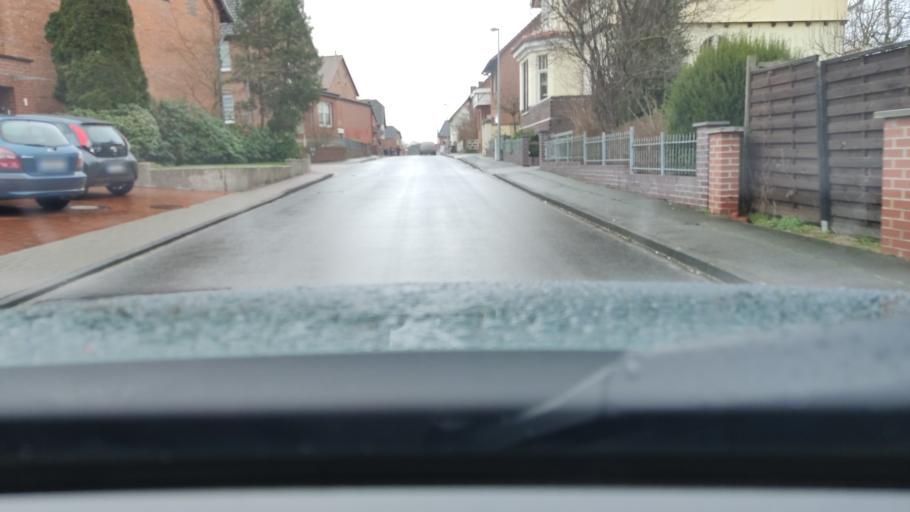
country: DE
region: Lower Saxony
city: Ilsede
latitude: 52.2671
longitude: 10.2253
